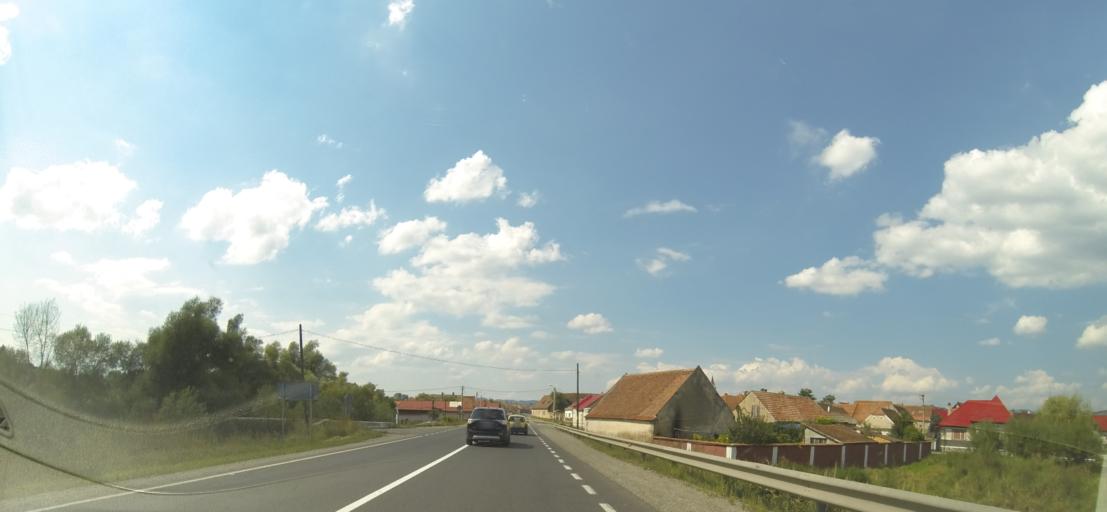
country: RO
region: Brasov
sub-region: Comuna Dumbravita
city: Dumbravita
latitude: 45.7648
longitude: 25.3758
